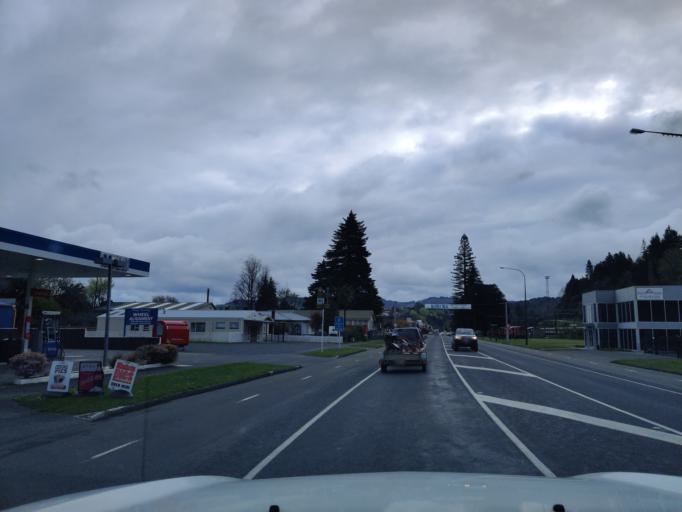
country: NZ
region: Waikato
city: Turangi
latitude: -38.8828
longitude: 175.2702
